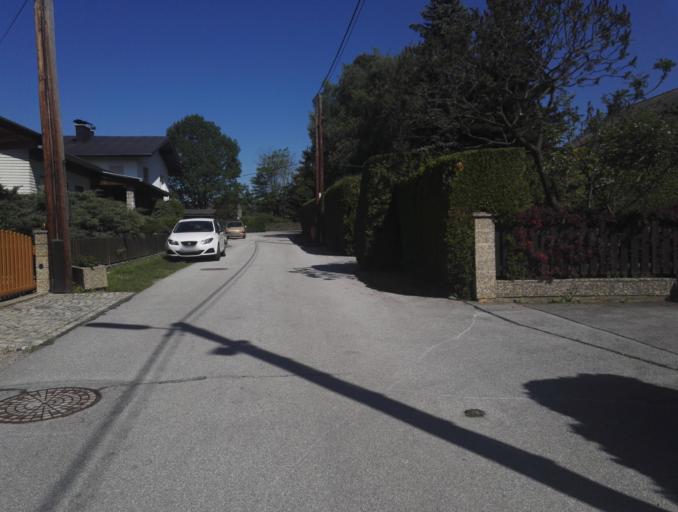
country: AT
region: Styria
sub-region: Politischer Bezirk Graz-Umgebung
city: Raaba
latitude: 47.0376
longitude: 15.5008
